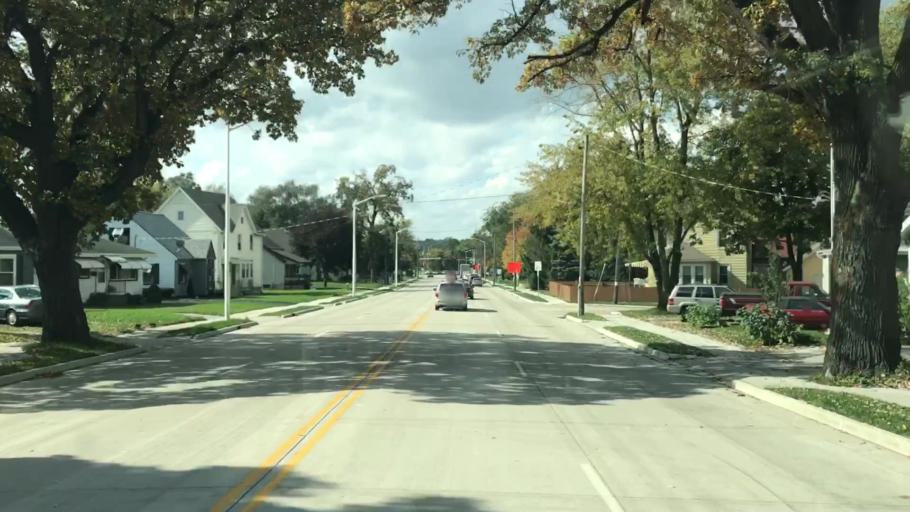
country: US
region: Wisconsin
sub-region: Waukesha County
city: Waukesha
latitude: 43.0229
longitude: -88.2148
